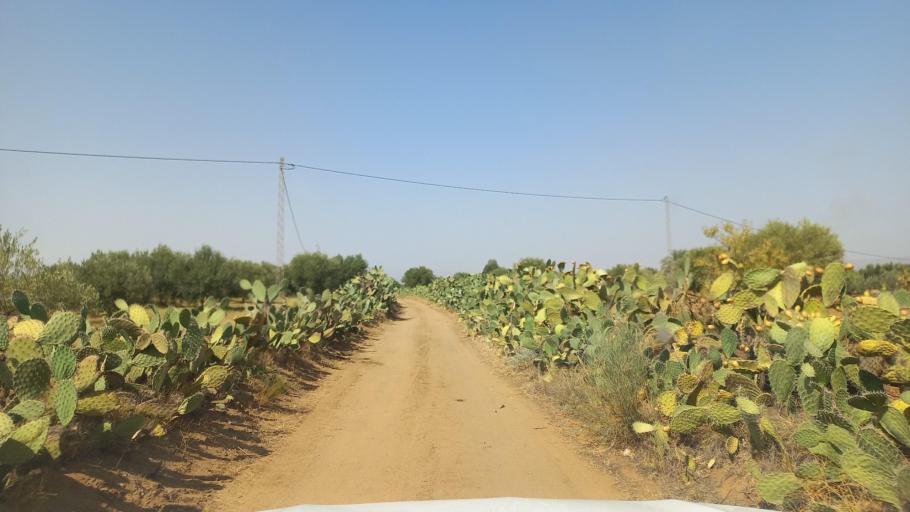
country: TN
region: Al Qasrayn
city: Kasserine
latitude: 35.2404
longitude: 9.0691
